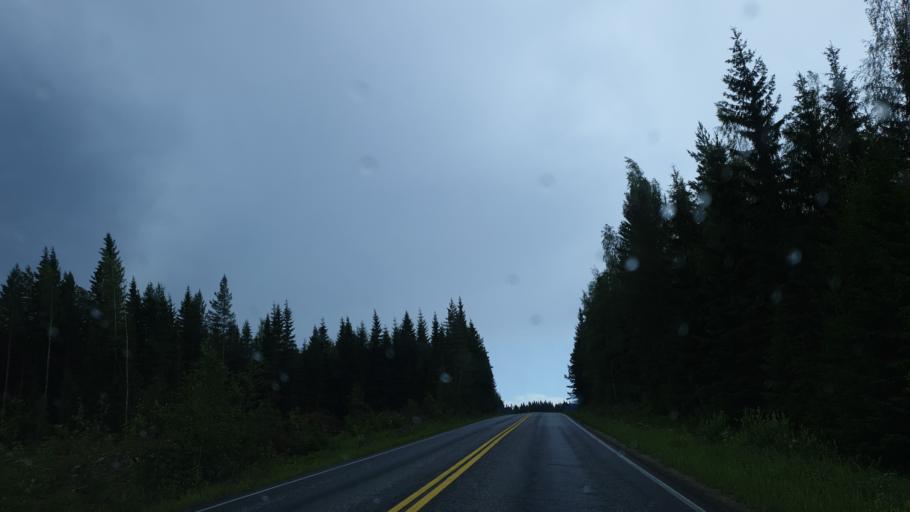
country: FI
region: Northern Savo
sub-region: Kuopio
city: Vehmersalmi
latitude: 62.9364
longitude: 27.9137
